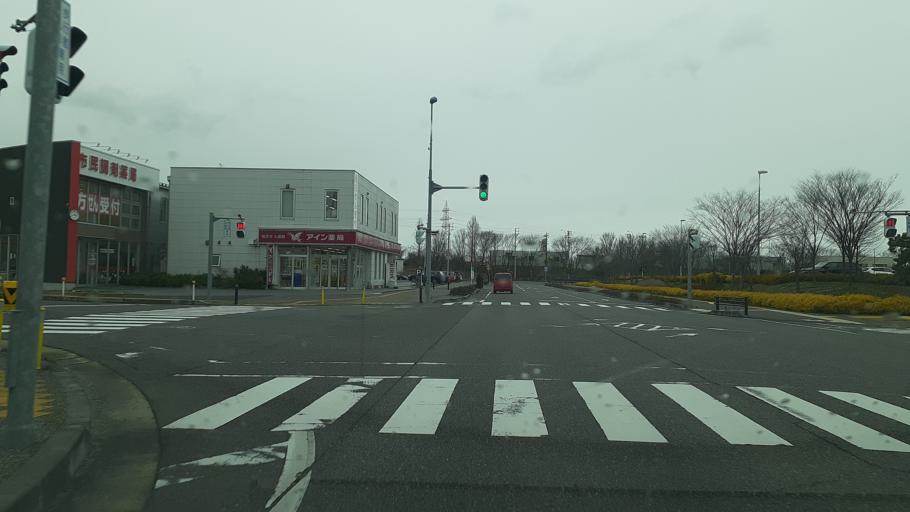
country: JP
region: Niigata
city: Niigata-shi
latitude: 37.8738
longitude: 139.0420
